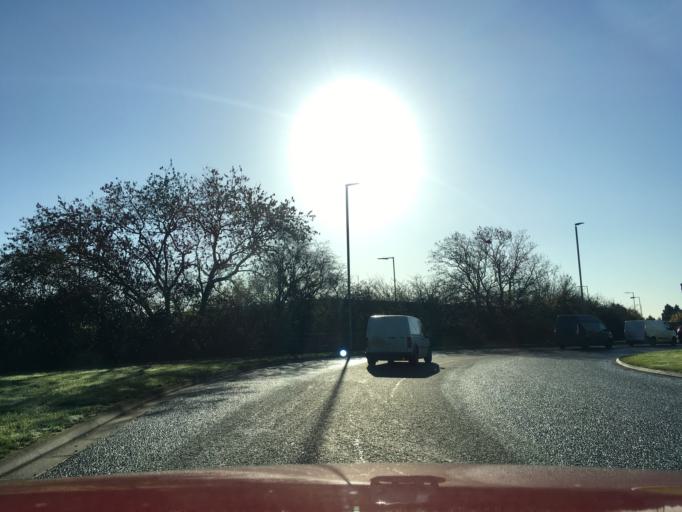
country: GB
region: England
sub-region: Somerset
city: Bridgwater
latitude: 51.1471
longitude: -2.9904
